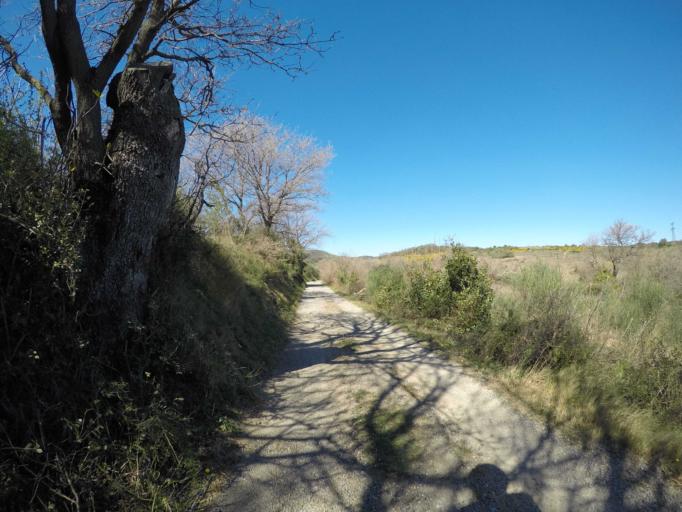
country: FR
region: Languedoc-Roussillon
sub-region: Departement des Pyrenees-Orientales
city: Millas
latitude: 42.7081
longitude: 2.6672
